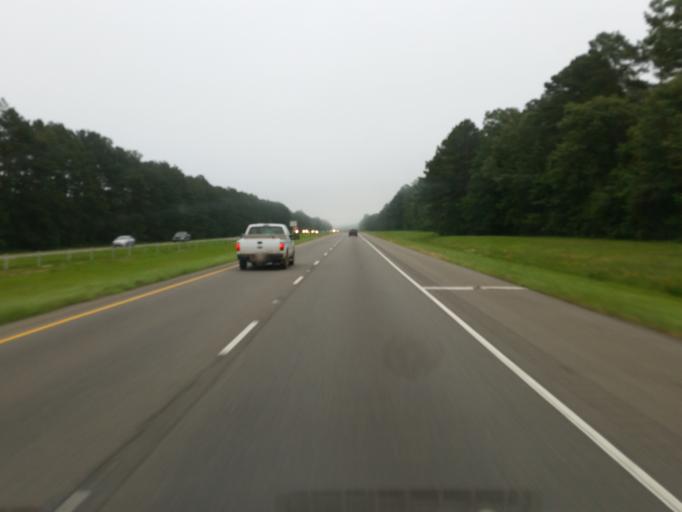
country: US
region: Louisiana
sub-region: Bossier Parish
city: Haughton
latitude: 32.5768
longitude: -93.4691
